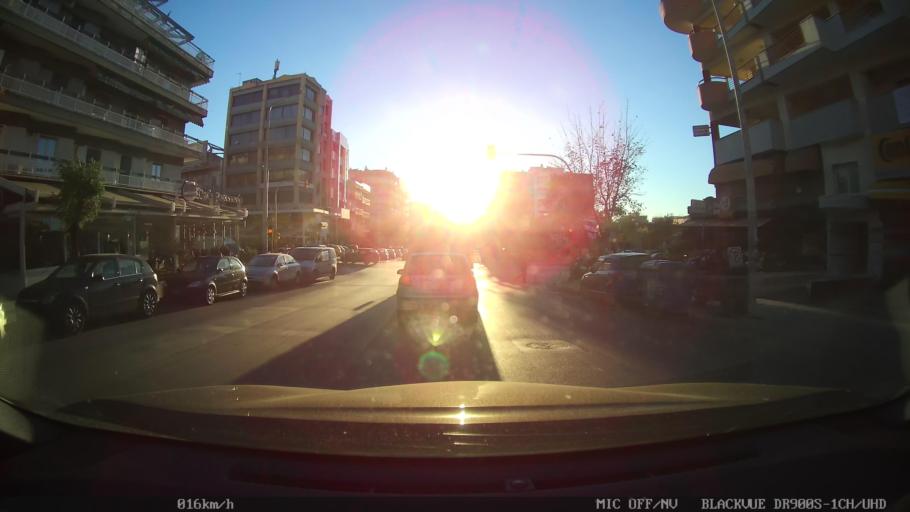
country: GR
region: Central Macedonia
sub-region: Nomos Thessalonikis
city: Triandria
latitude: 40.6129
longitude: 22.9648
